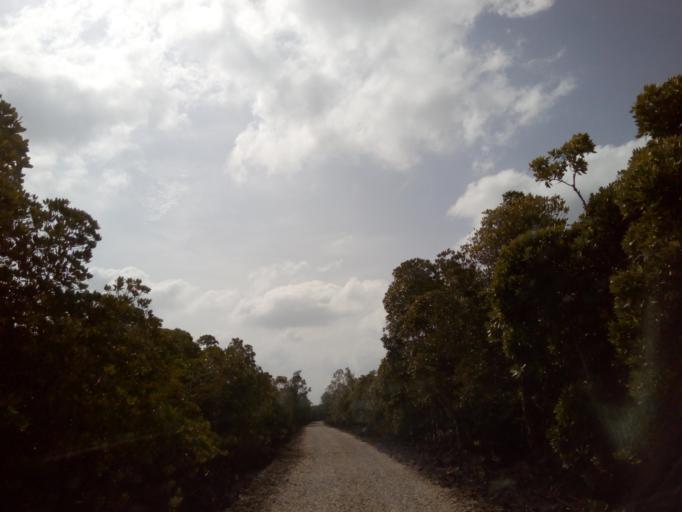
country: TZ
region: Zanzibar Central/South
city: Mahonda
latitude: -6.3151
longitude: 39.3844
